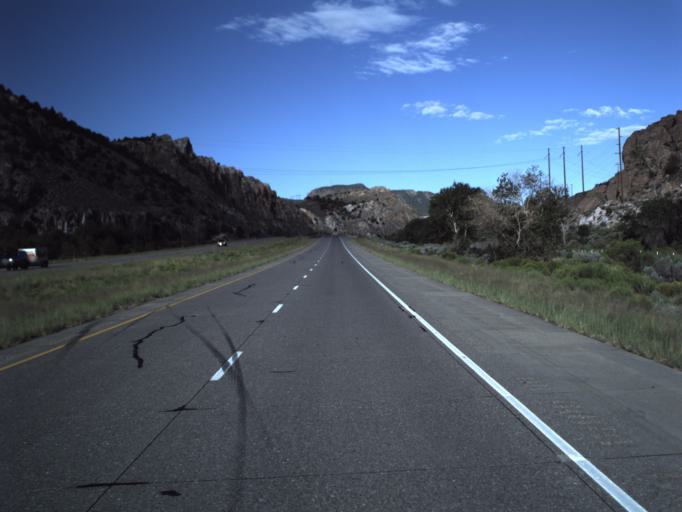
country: US
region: Utah
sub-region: Sevier County
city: Monroe
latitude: 38.5792
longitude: -112.3102
